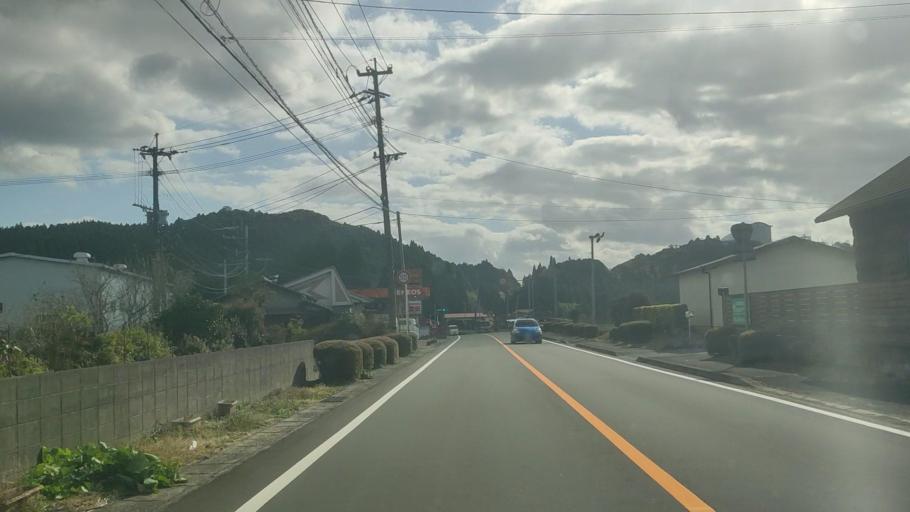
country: JP
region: Kagoshima
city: Kajiki
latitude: 31.8333
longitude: 130.6878
